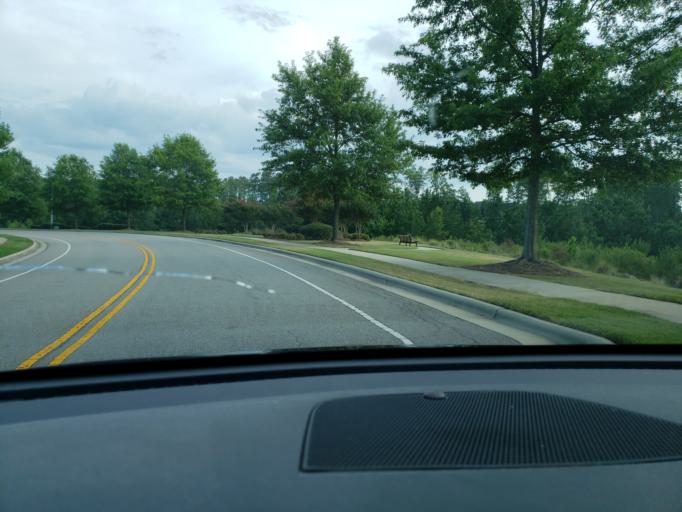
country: US
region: North Carolina
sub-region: Wake County
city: Green Level
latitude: 35.8295
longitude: -78.9134
